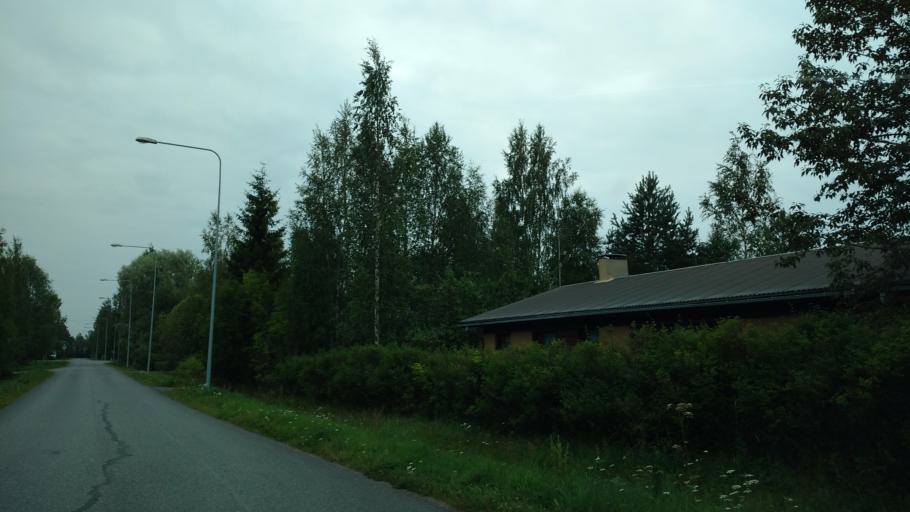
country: FI
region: Haeme
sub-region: Forssa
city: Ypaejae
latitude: 60.8081
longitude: 23.2772
